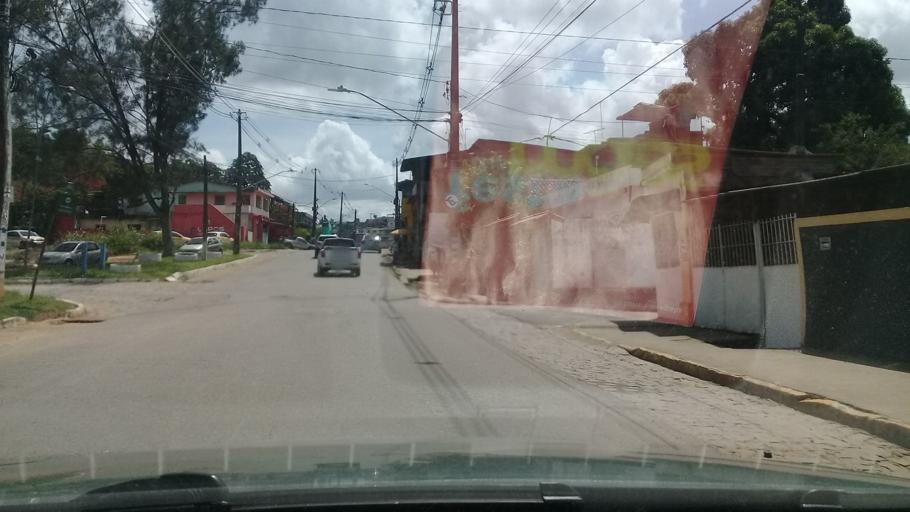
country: BR
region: Pernambuco
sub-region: Jaboatao Dos Guararapes
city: Jaboatao dos Guararapes
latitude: -8.1036
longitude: -35.0186
